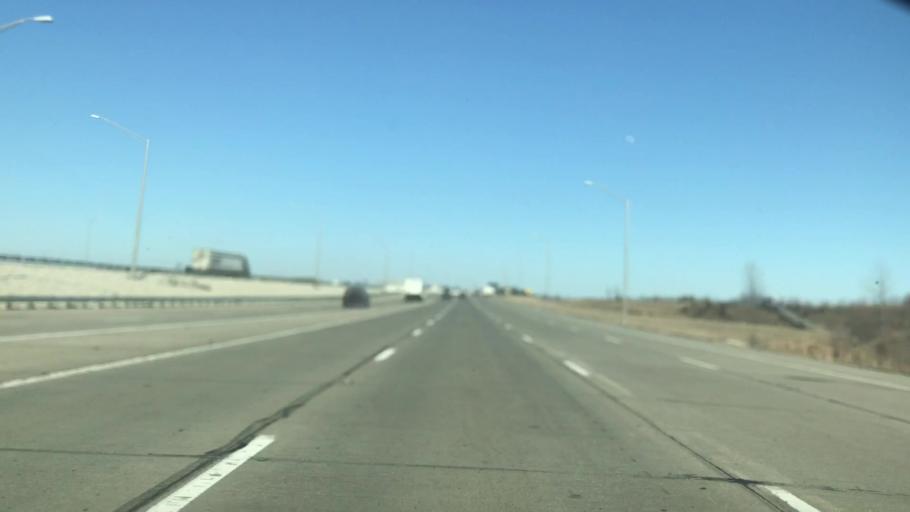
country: US
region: Indiana
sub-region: Hendricks County
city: Plainfield
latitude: 39.6928
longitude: -86.3086
